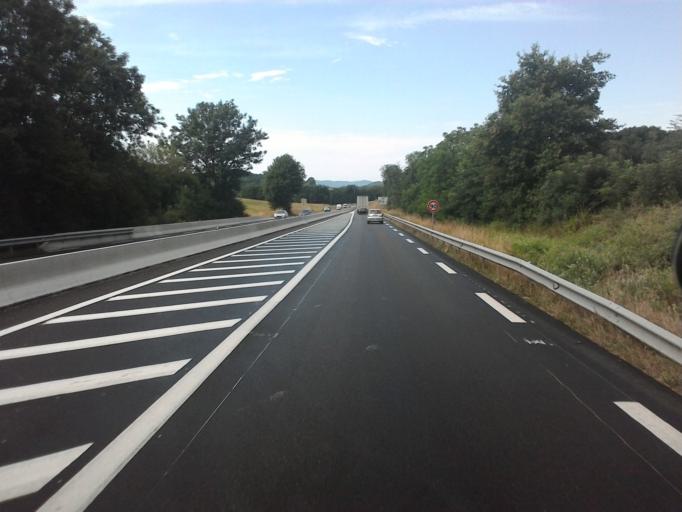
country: FR
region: Franche-Comte
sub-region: Departement du Jura
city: Lons-le-Saunier
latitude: 46.7117
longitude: 5.5522
